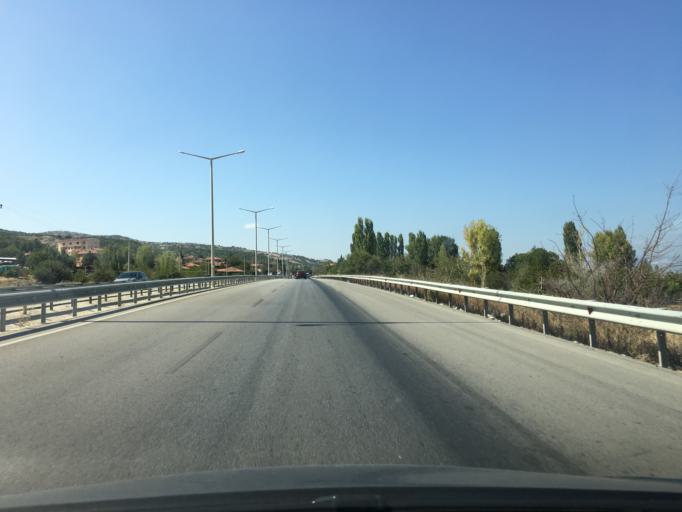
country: TR
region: Burdur
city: Burdur
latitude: 37.7612
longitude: 30.3455
